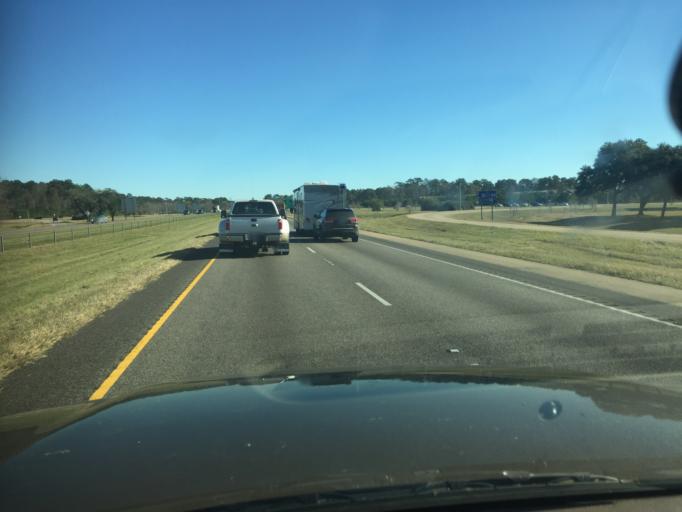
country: US
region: Louisiana
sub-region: Saint Tammany Parish
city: Covington
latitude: 30.4426
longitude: -90.1277
